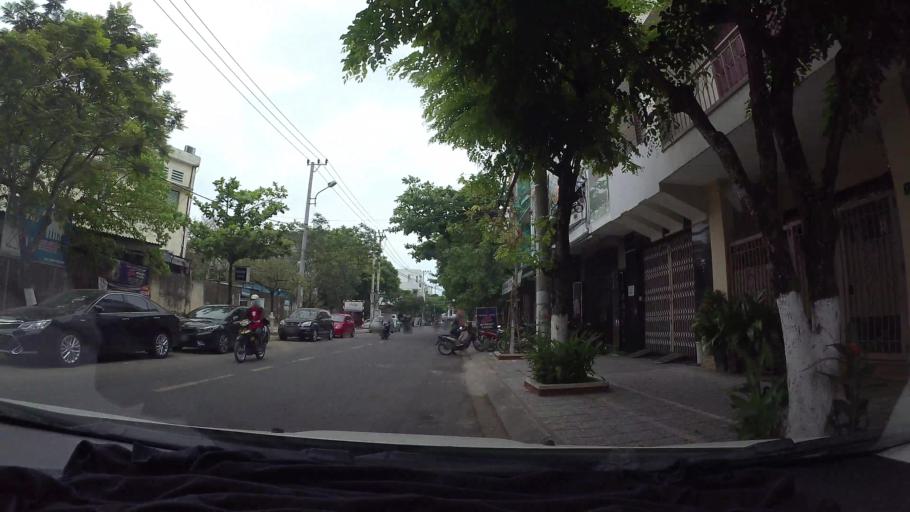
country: VN
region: Da Nang
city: Da Nang
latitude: 16.0782
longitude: 108.2142
